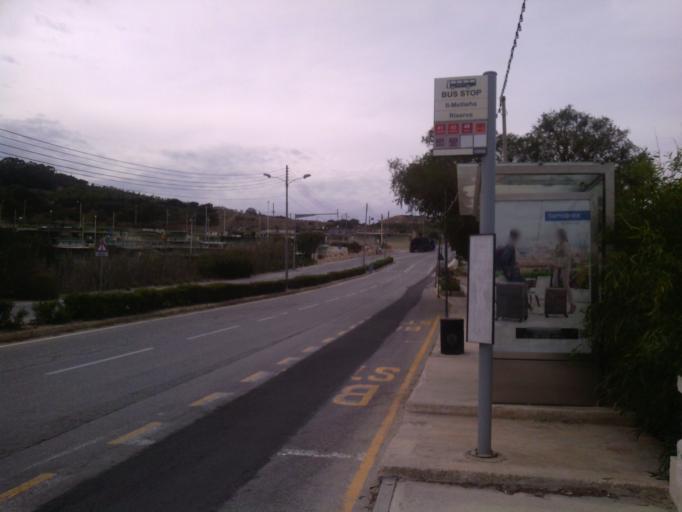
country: MT
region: Il-Mellieha
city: Mellieha
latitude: 35.9728
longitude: 14.3494
